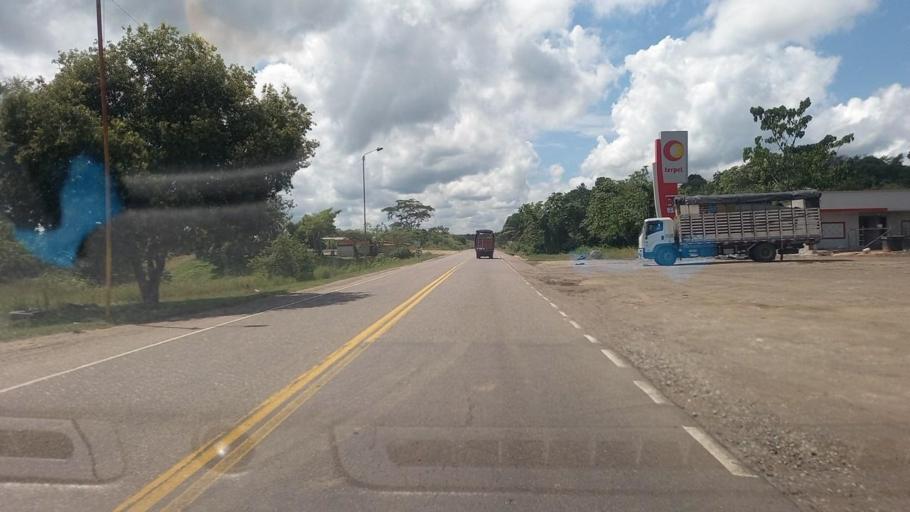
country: CO
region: Santander
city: Barrancabermeja
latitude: 7.0103
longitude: -73.6788
